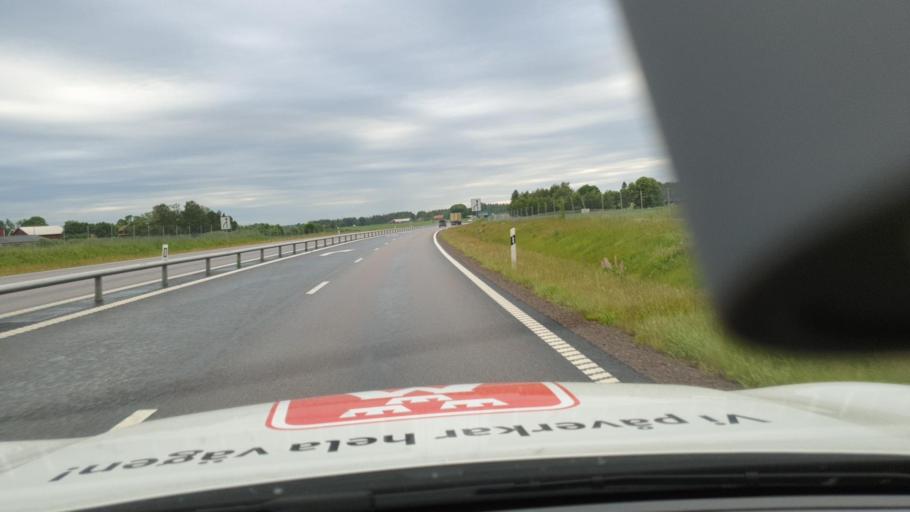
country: SE
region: Vaestra Goetaland
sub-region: Gullspangs Kommun
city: Hova
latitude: 58.8275
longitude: 14.1686
